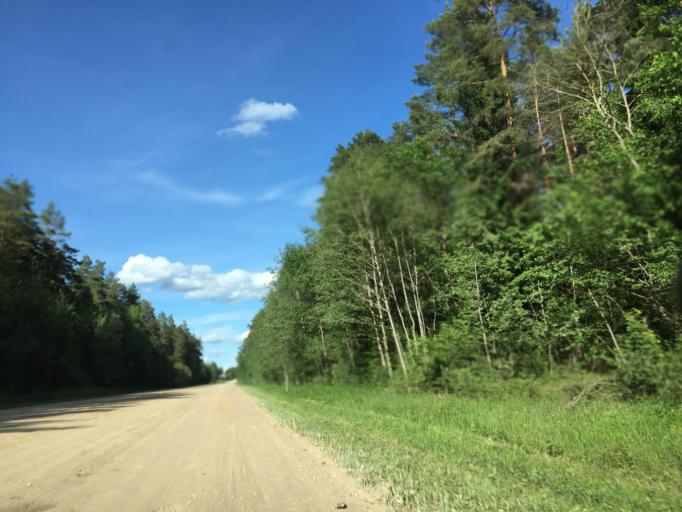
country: LV
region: Vecumnieki
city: Vecumnieki
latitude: 56.4466
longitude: 24.5821
